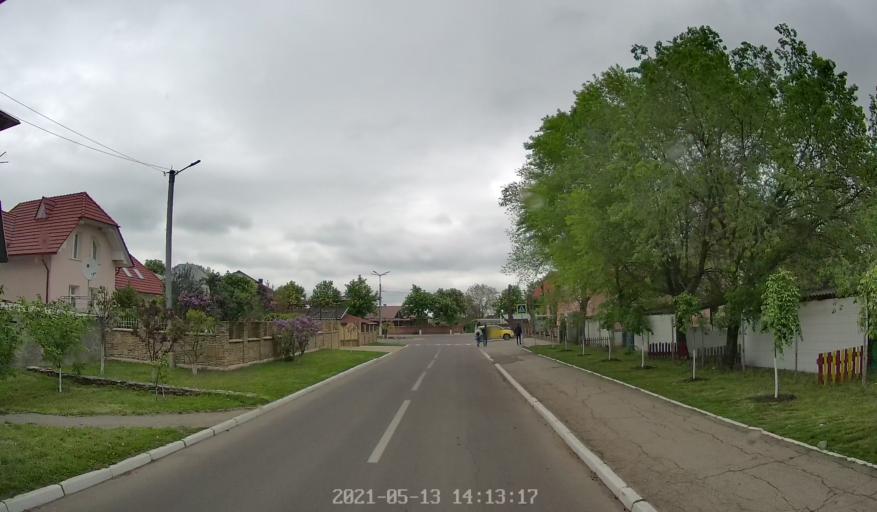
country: MD
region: Chisinau
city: Stauceni
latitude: 47.0896
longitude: 28.8672
